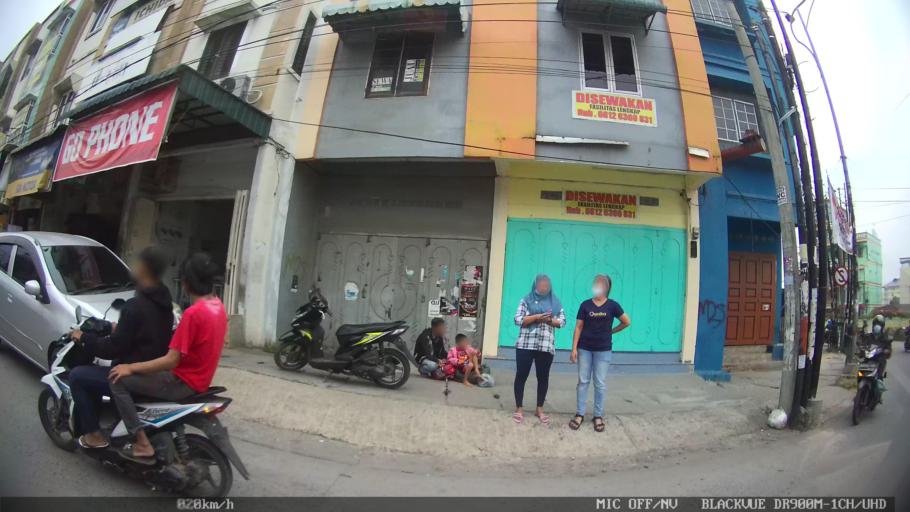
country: ID
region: North Sumatra
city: Deli Tua
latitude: 3.5378
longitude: 98.6841
